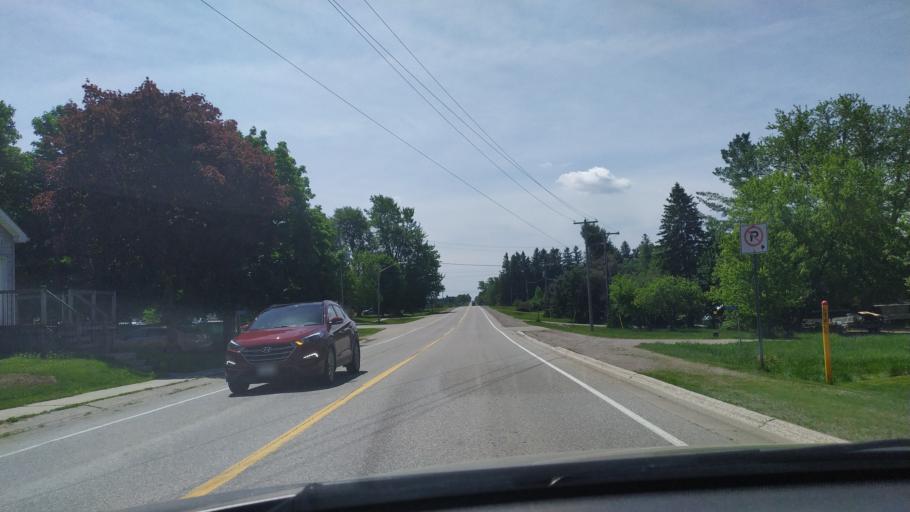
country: CA
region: Ontario
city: Dorchester
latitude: 43.1387
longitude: -81.0300
